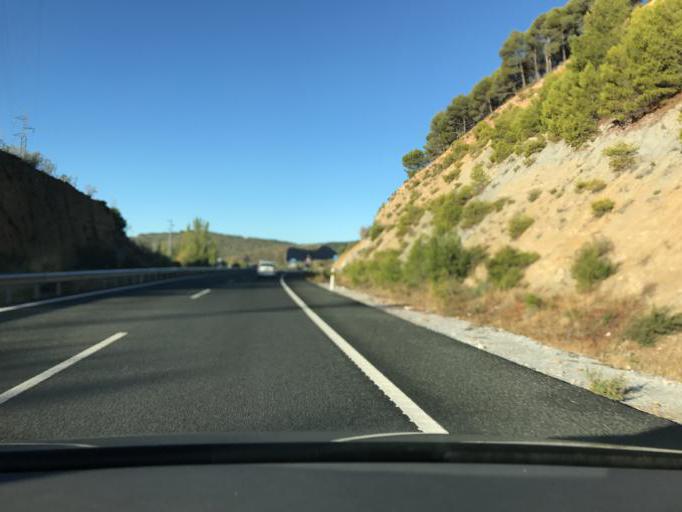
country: ES
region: Andalusia
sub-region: Provincia de Granada
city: Huetor Santillan
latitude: 37.2277
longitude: -3.5129
